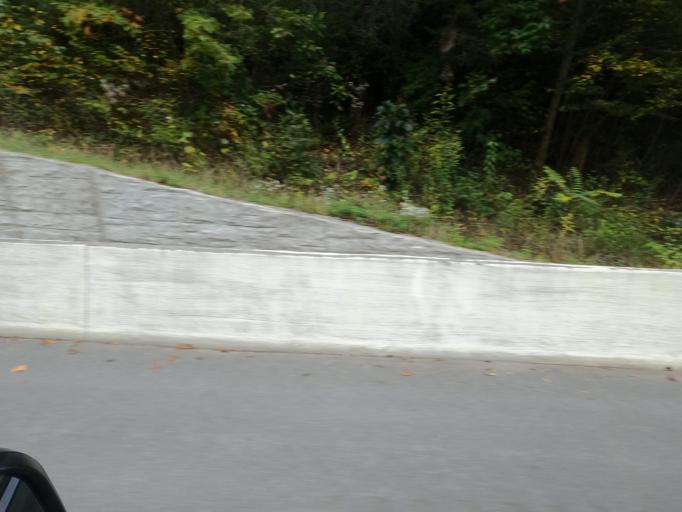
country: US
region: Tennessee
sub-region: Carter County
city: Elizabethton
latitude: 36.2684
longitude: -82.2301
